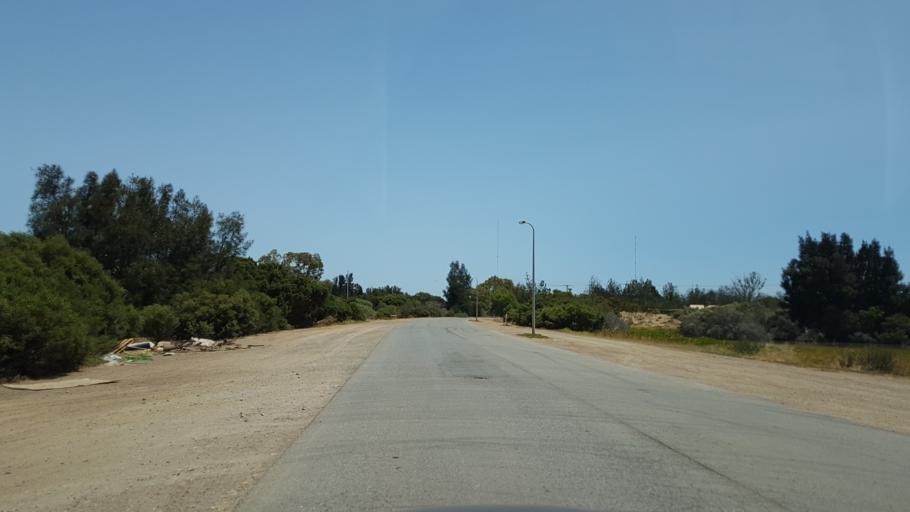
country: AU
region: South Australia
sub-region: Port Adelaide Enfield
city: Enfield
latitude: -34.8309
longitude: 138.5826
